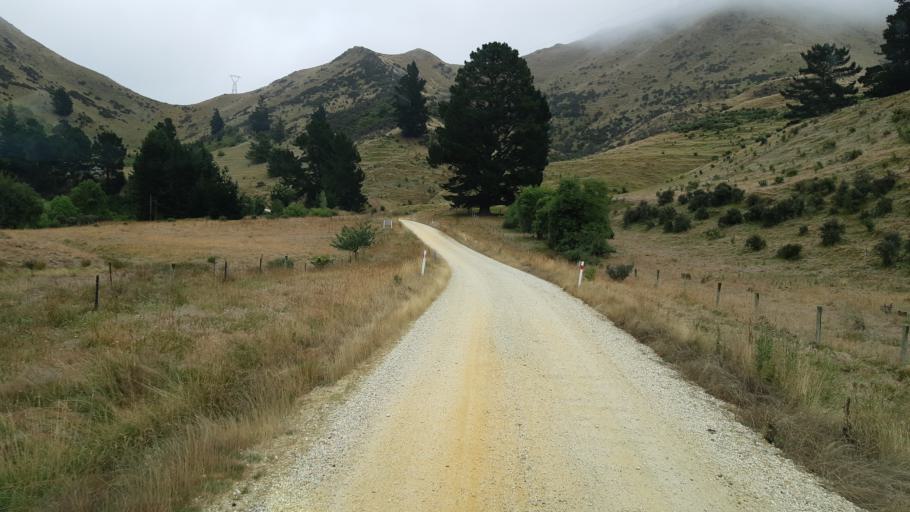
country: NZ
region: Otago
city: Oamaru
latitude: -44.9537
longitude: 170.4735
